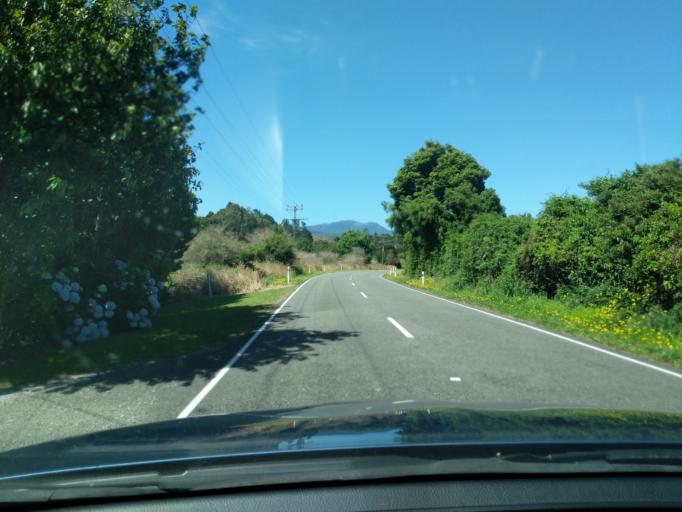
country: NZ
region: Tasman
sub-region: Tasman District
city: Takaka
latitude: -40.7246
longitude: 172.6380
